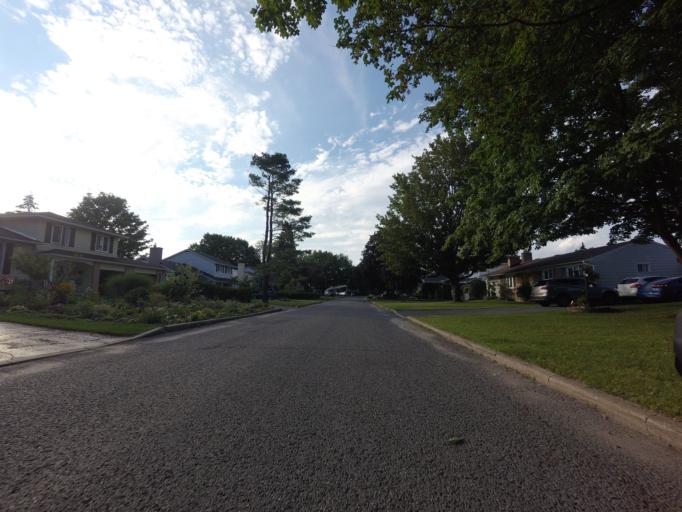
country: CA
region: Ontario
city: Bells Corners
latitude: 45.2827
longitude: -75.7651
